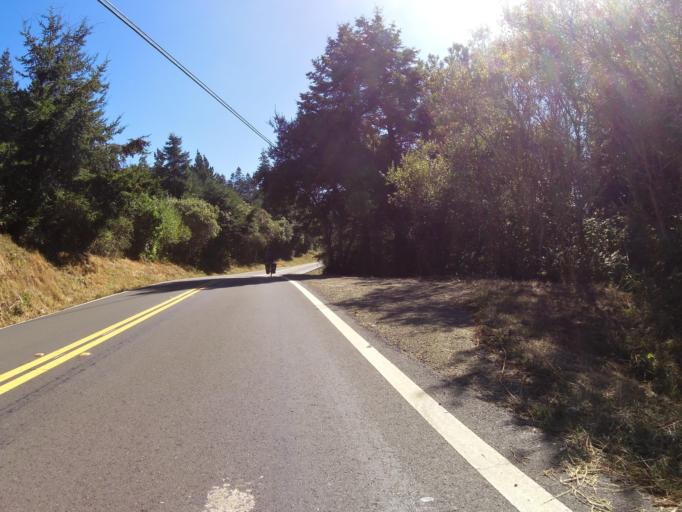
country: US
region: California
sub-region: Mendocino County
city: Fort Bragg
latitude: 39.6305
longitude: -123.7825
